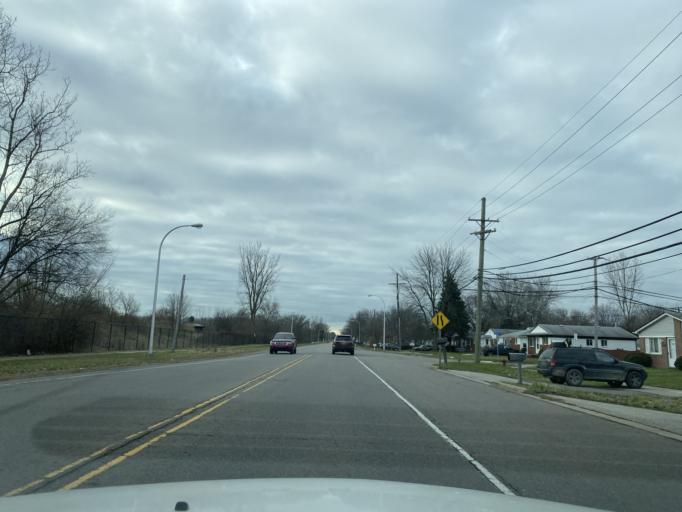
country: US
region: Michigan
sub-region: Wayne County
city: Taylor
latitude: 42.2071
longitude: -83.2876
